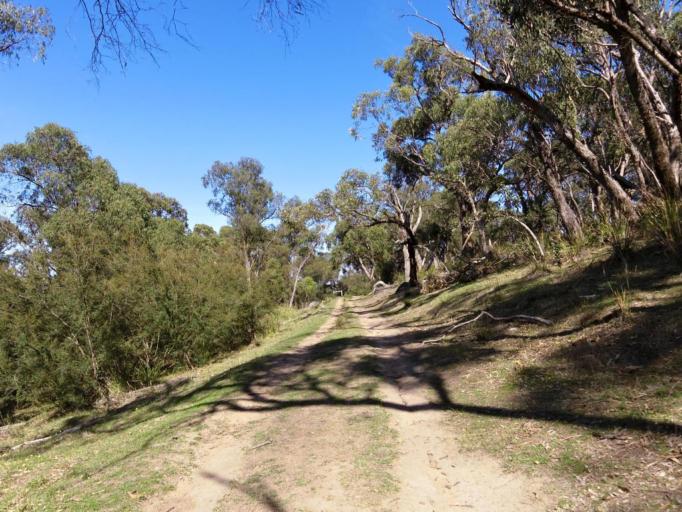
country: AU
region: Victoria
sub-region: Yarra Ranges
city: Lysterfield
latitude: -37.9364
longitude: 145.2911
